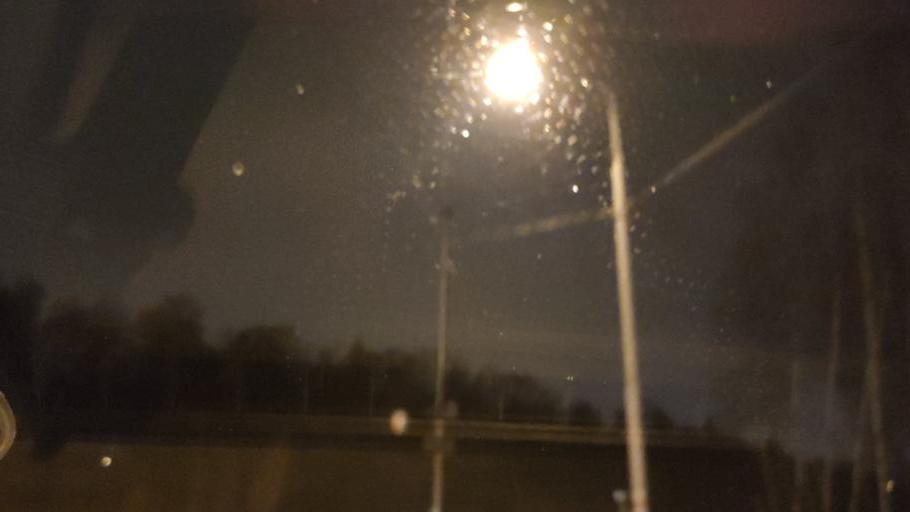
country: RU
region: Moscow
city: Annino
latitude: 55.5392
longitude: 37.6139
